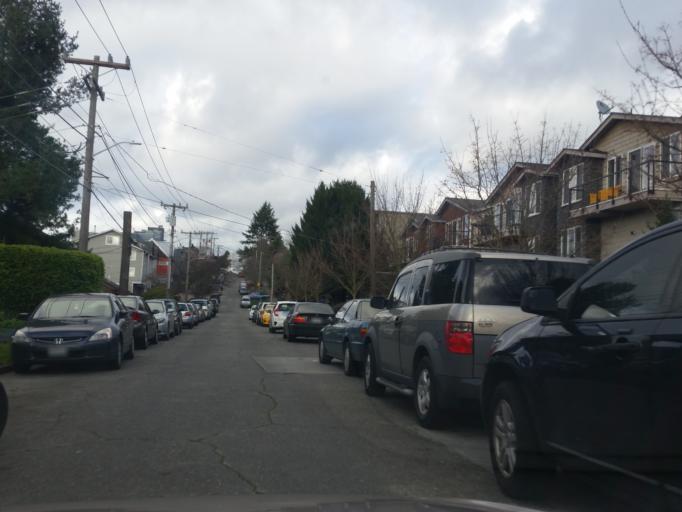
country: US
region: Washington
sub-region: King County
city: Seattle
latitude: 47.6592
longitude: -122.3554
